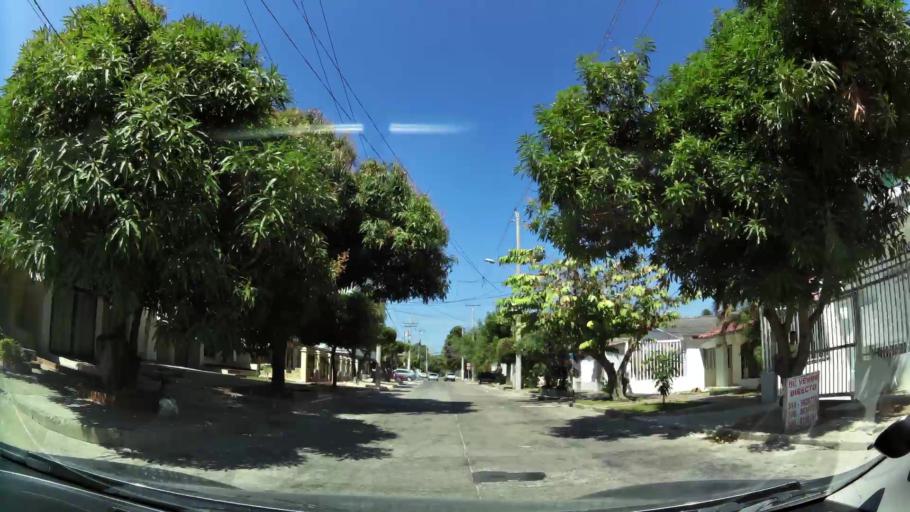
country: CO
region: Atlantico
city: Barranquilla
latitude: 11.0096
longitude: -74.7969
